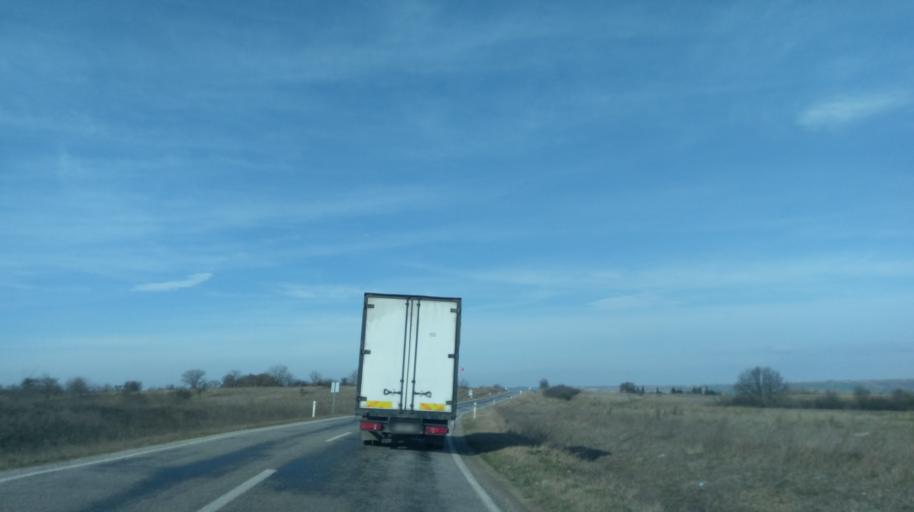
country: TR
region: Edirne
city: Copkoy
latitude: 41.3069
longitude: 26.8433
